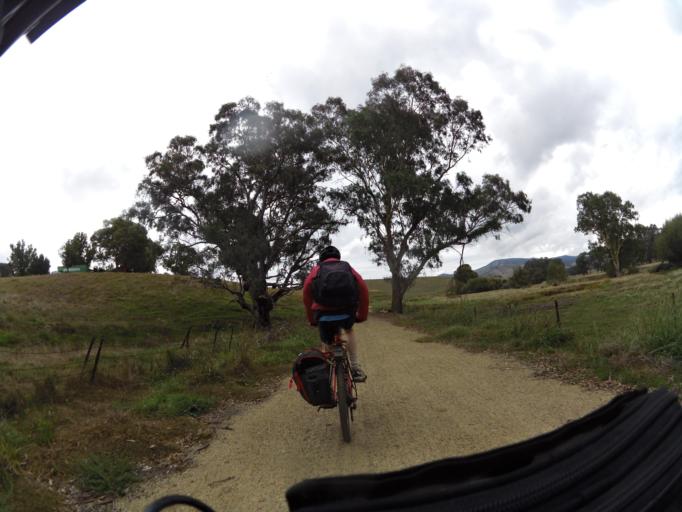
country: AU
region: New South Wales
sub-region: Albury Municipality
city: East Albury
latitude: -36.1948
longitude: 147.3073
